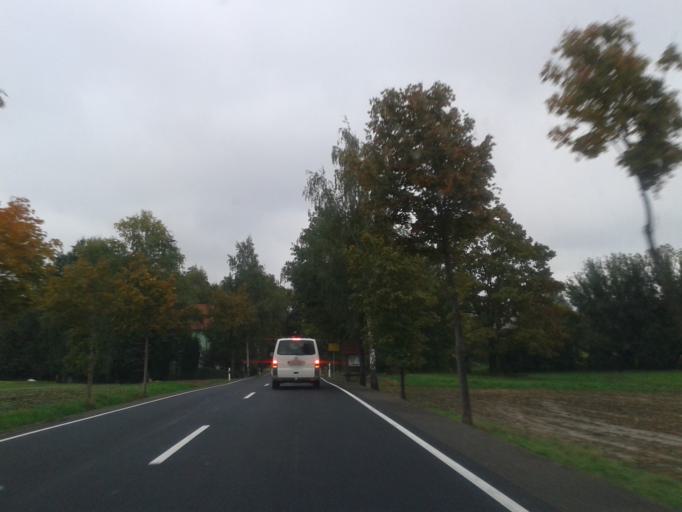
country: DE
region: Saxony
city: Wilsdruff
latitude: 51.0505
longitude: 13.4645
